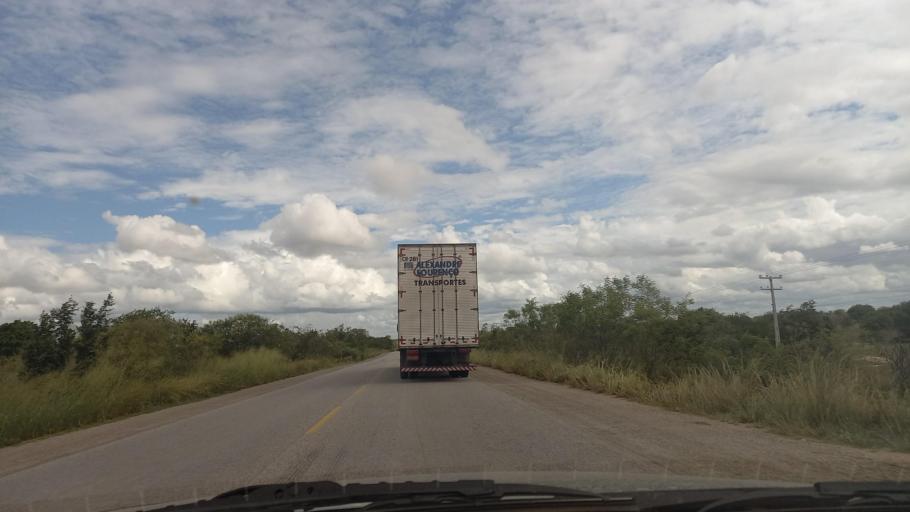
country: BR
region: Pernambuco
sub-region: Cachoeirinha
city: Cachoeirinha
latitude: -8.3925
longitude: -36.1791
